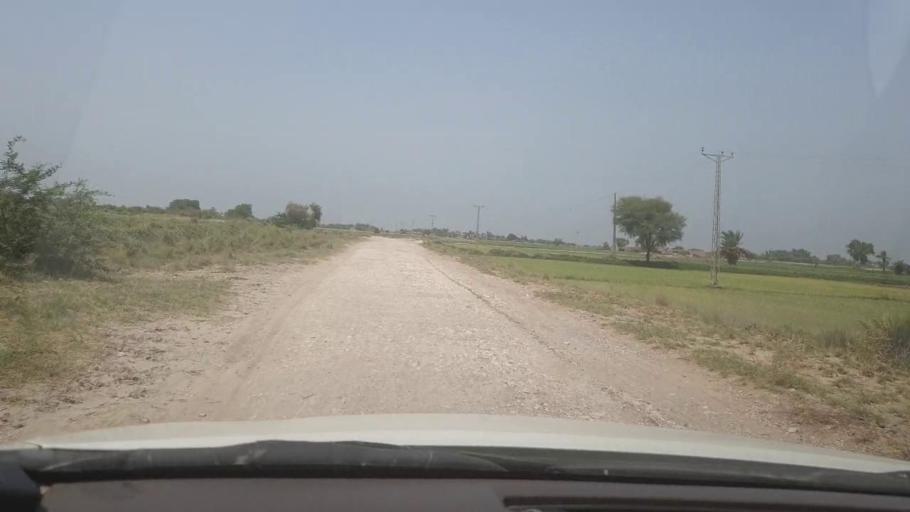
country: PK
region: Sindh
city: Shikarpur
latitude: 27.9379
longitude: 68.5752
